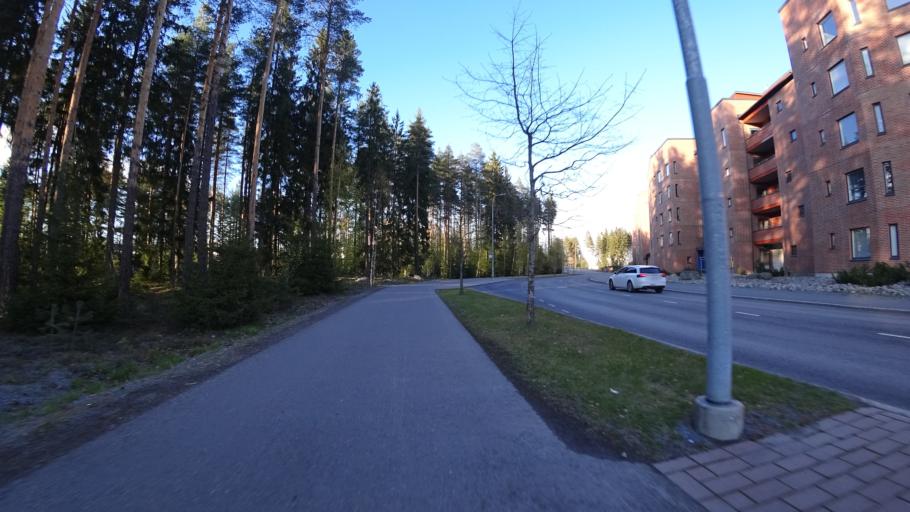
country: FI
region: Pirkanmaa
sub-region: Tampere
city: Pirkkala
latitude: 61.5006
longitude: 23.6067
